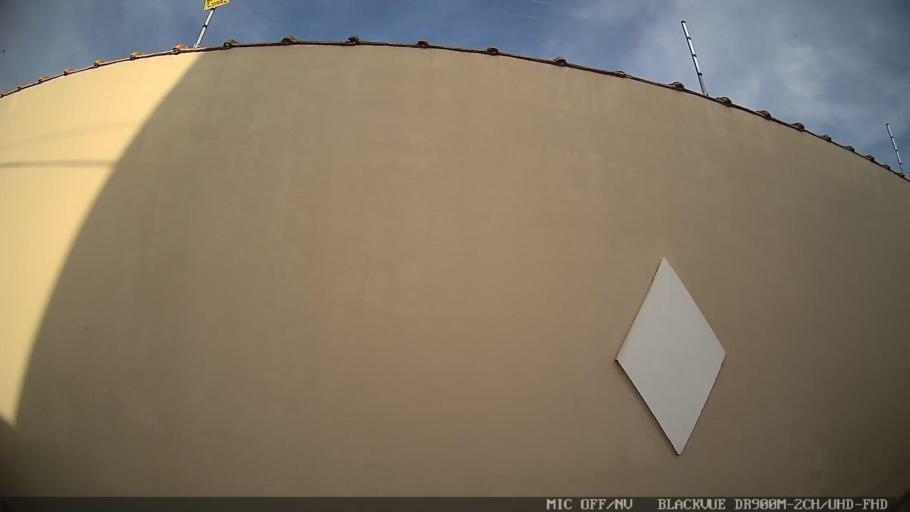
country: BR
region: Sao Paulo
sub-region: Itanhaem
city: Itanhaem
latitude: -24.1609
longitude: -46.7660
